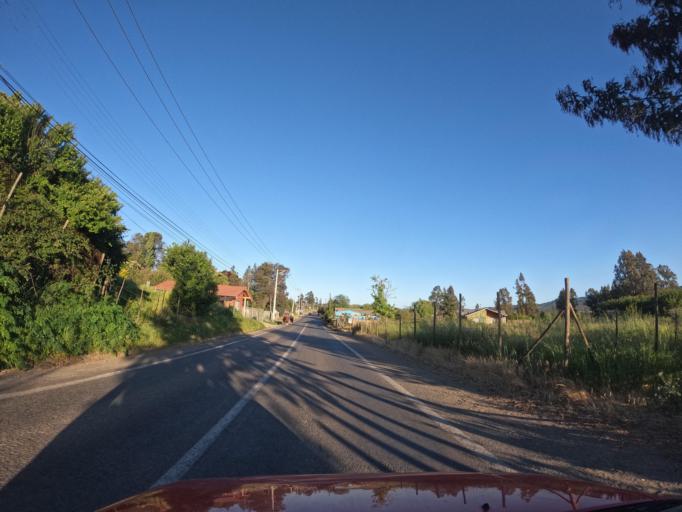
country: CL
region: Maule
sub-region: Provincia de Talca
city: Talca
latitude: -34.9949
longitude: -71.9732
